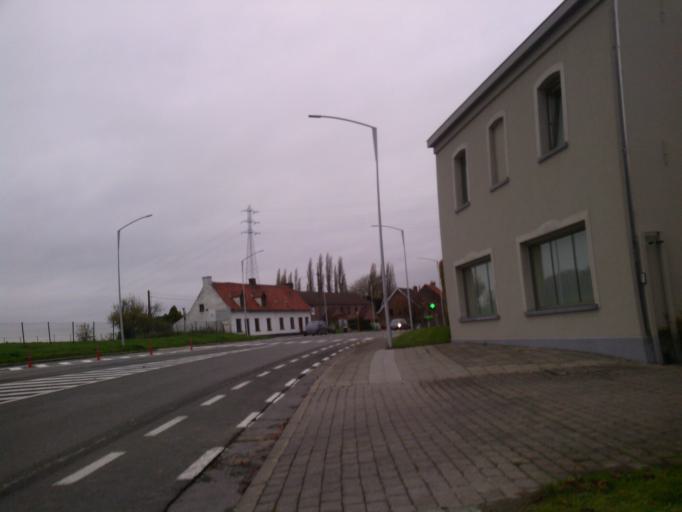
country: BE
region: Wallonia
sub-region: Province du Hainaut
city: Mouscron
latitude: 50.7609
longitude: 3.2194
